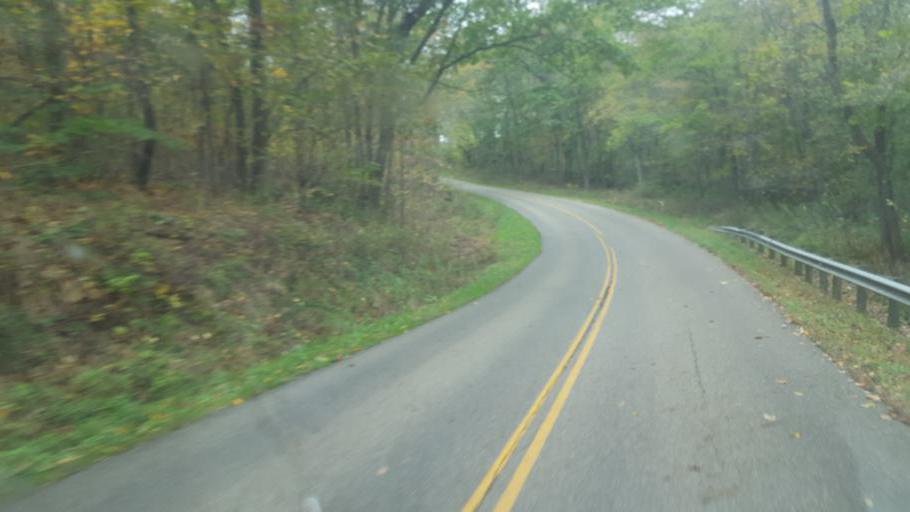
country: US
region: Ohio
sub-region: Carroll County
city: Carrollton
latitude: 40.5317
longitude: -81.1408
